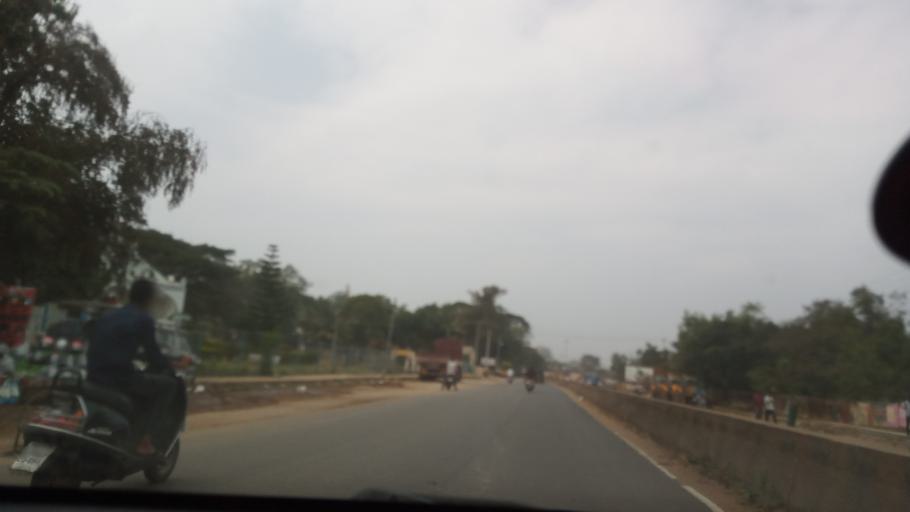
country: IN
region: Karnataka
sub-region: Chamrajnagar
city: Chamrajnagar
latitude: 11.9187
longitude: 76.9403
